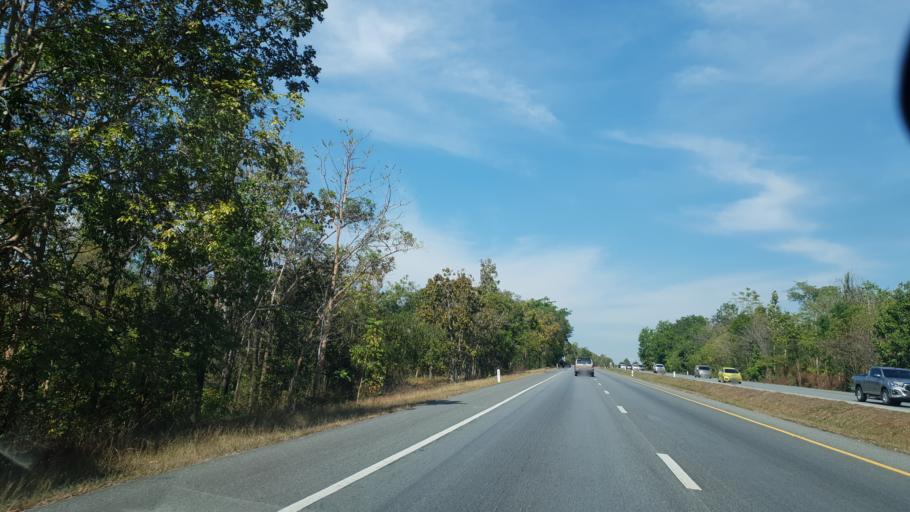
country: TH
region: Uttaradit
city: Thong Saen Khan
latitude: 17.4189
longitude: 100.2267
